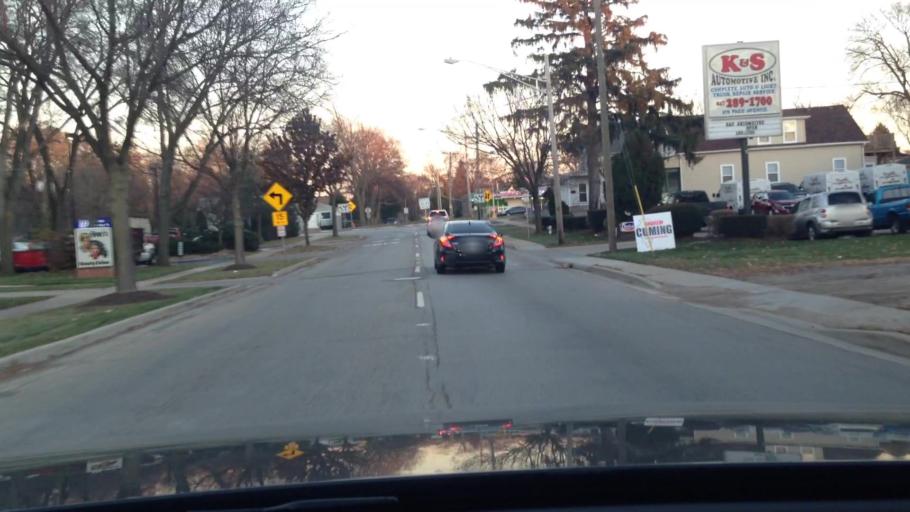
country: US
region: Illinois
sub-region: Kane County
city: Elgin
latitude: 42.0542
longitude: -88.2691
